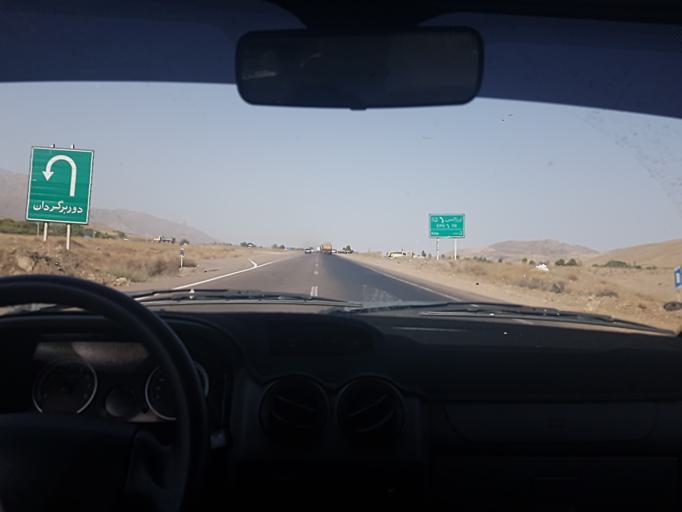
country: IR
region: East Azerbaijan
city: Marand
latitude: 38.3400
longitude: 45.8503
